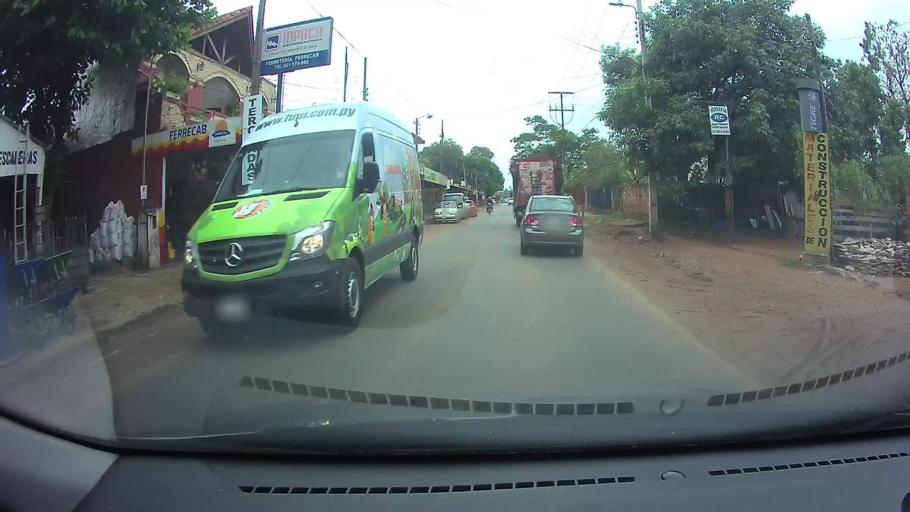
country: PY
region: Central
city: San Lorenzo
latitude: -25.3251
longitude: -57.5010
